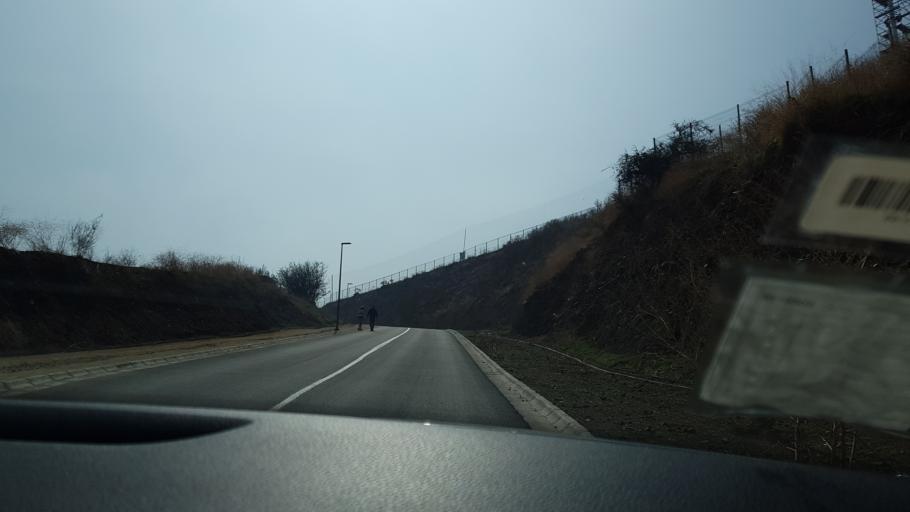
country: CL
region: Santiago Metropolitan
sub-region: Provincia de Santiago
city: Villa Presidente Frei, Nunoa, Santiago, Chile
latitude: -33.4807
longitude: -70.5172
